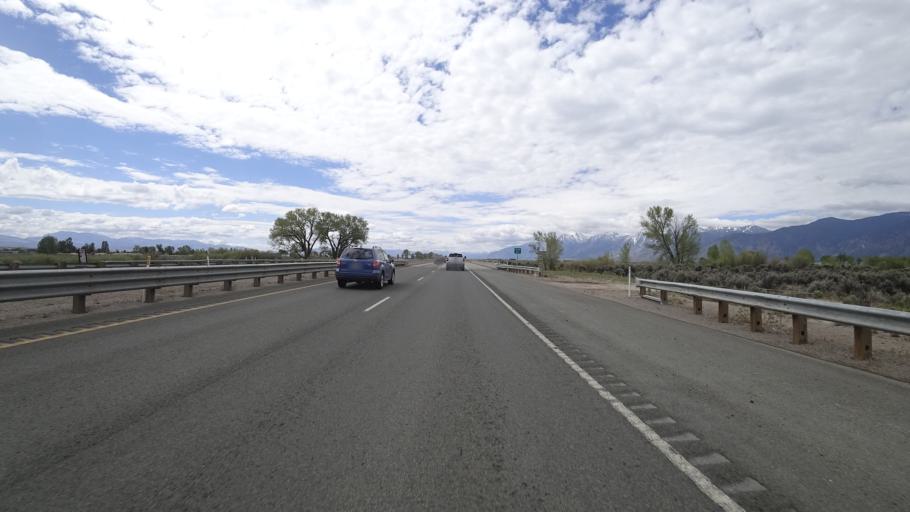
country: US
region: Nevada
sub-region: Douglas County
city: Indian Hills
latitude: 39.0489
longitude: -119.7801
